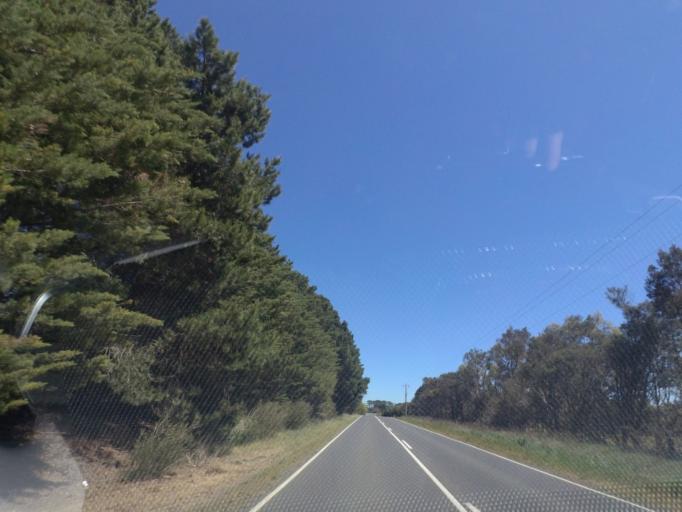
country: AU
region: Victoria
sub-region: Hume
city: Sunbury
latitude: -37.2849
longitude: 144.7627
